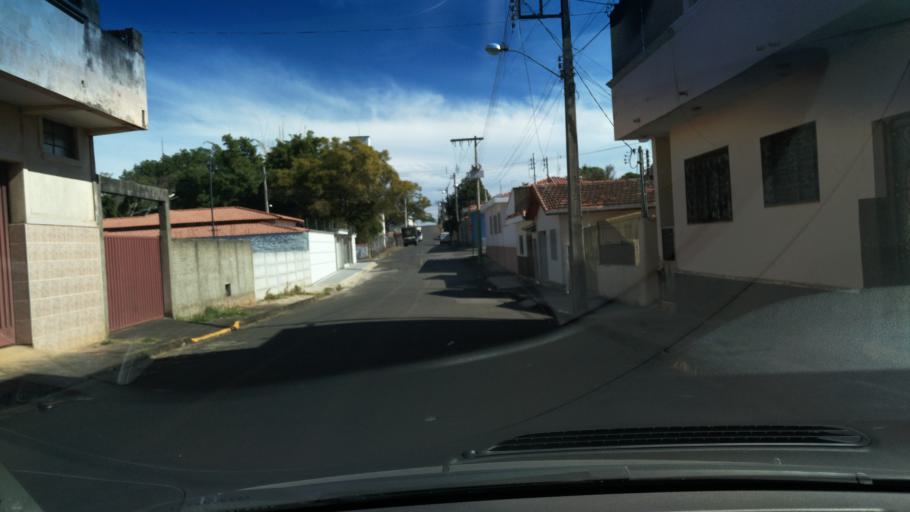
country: BR
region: Minas Gerais
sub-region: Andradas
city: Andradas
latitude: -22.0738
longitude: -46.5705
